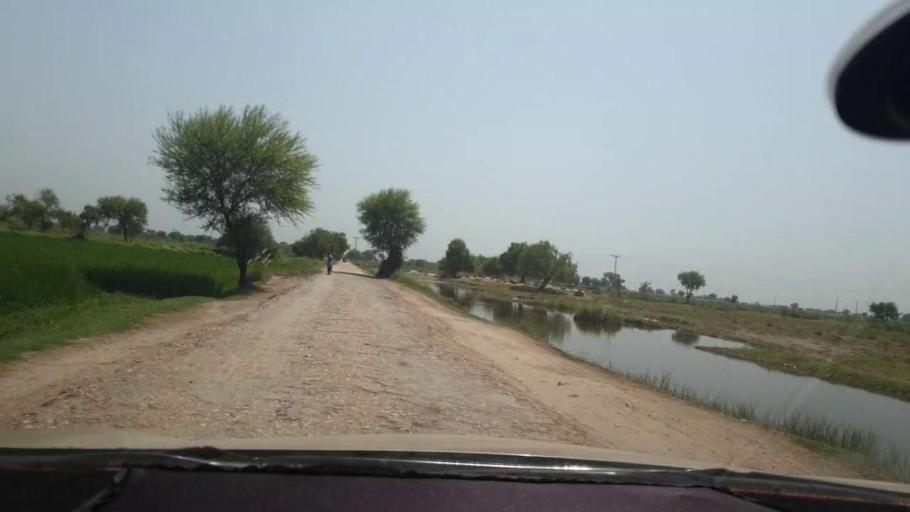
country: PK
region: Sindh
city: Kambar
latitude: 27.6323
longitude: 67.9326
